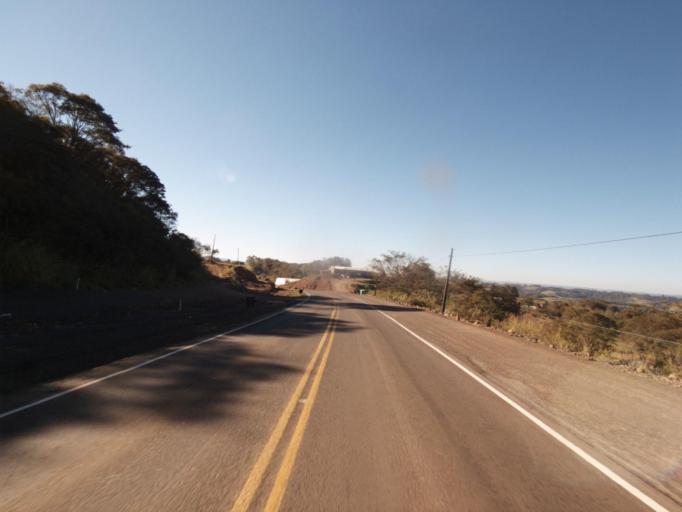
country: AR
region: Misiones
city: Bernardo de Irigoyen
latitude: -26.6915
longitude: -53.5147
